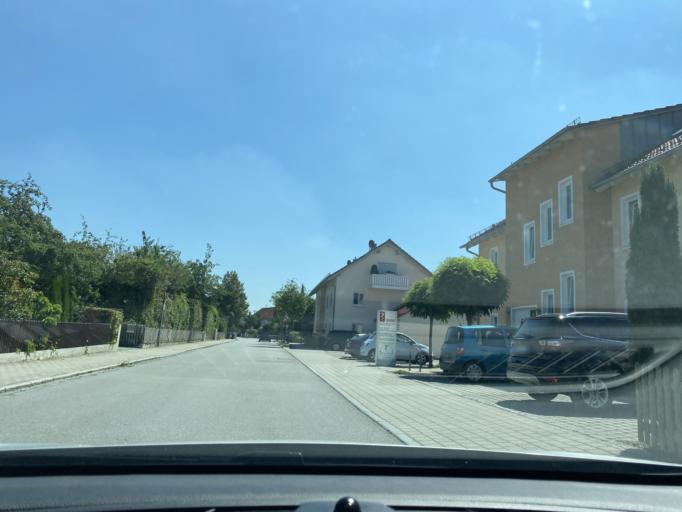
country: DE
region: Bavaria
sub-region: Upper Bavaria
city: Moosinning
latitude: 48.2747
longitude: 11.8392
